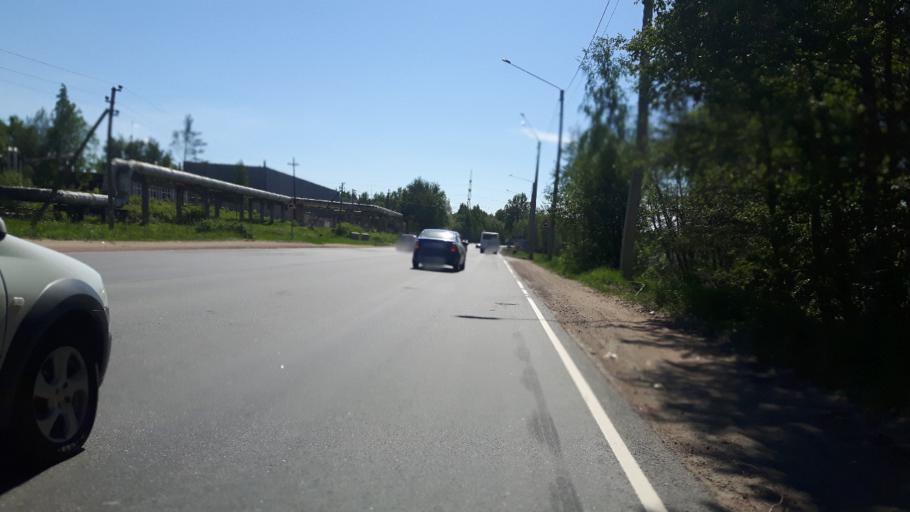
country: RU
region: Leningrad
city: Sosnovyy Bor
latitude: 59.8605
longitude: 29.0643
